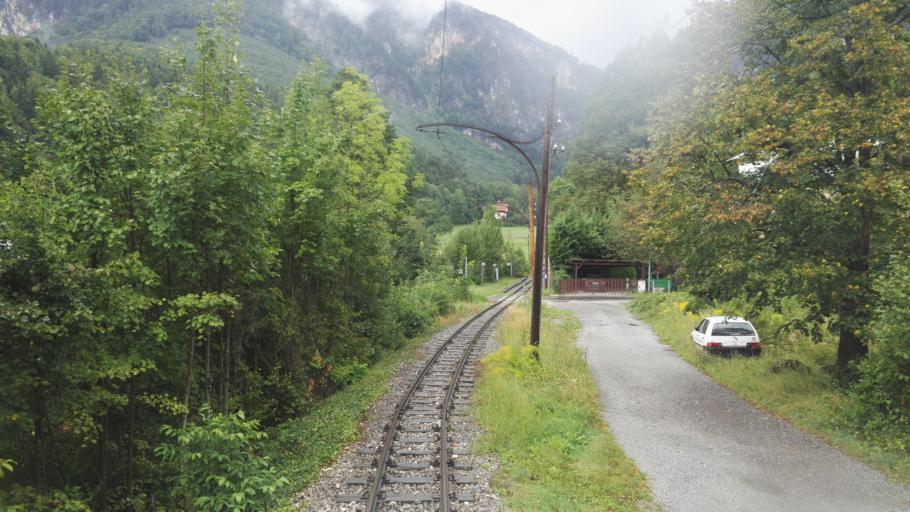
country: AT
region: Lower Austria
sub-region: Politischer Bezirk Neunkirchen
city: Reichenau an der Rax
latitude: 47.6986
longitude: 15.8458
